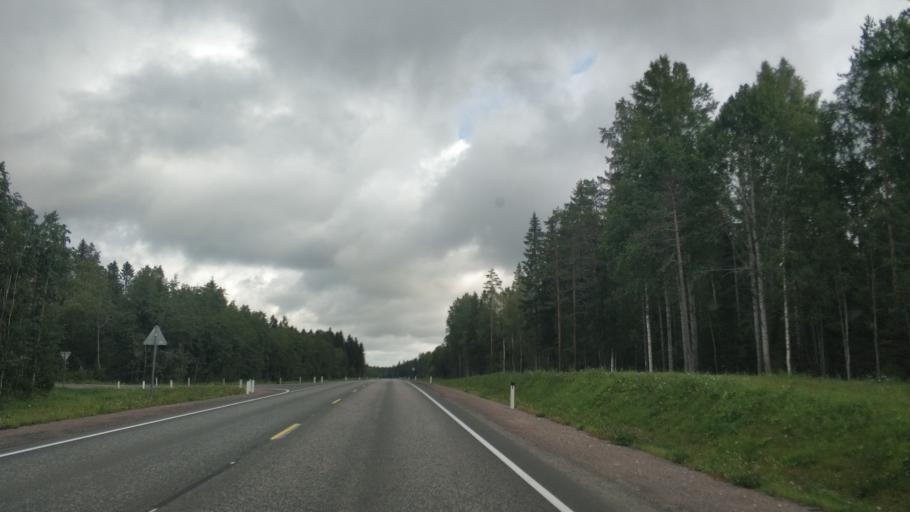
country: RU
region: Republic of Karelia
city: Khelyulya
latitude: 61.8427
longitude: 30.6463
